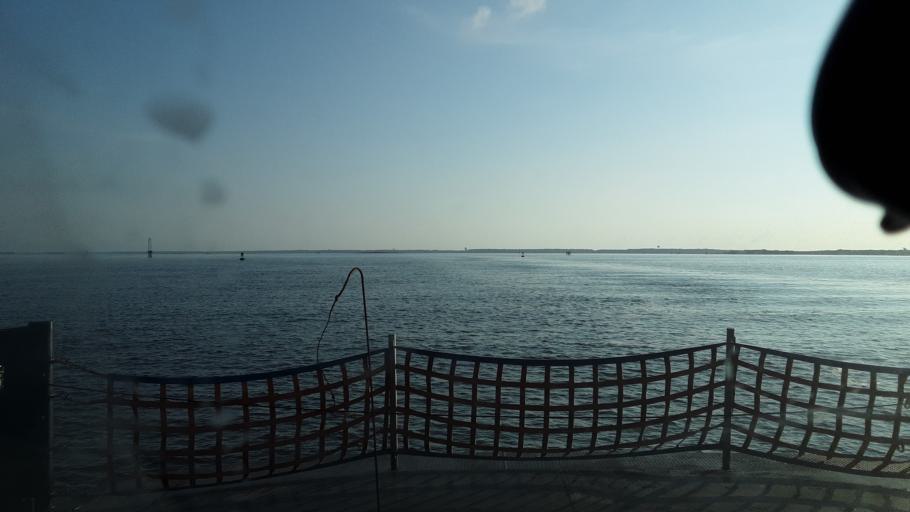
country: US
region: North Carolina
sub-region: New Hanover County
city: Kure Beach
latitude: 33.9562
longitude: -77.9577
